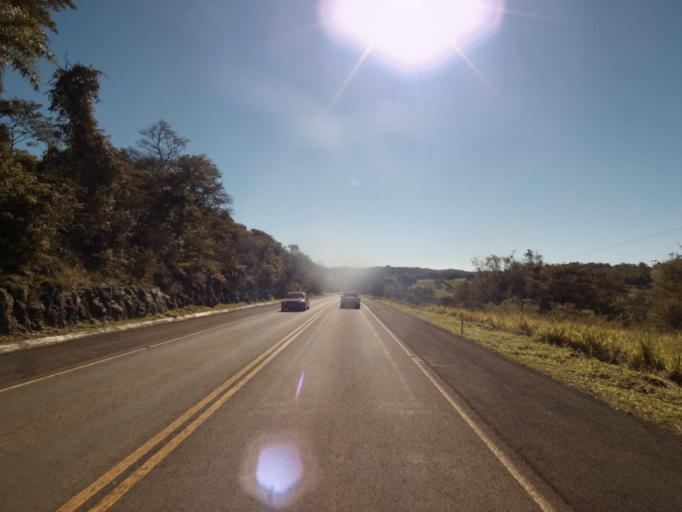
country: AR
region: Misiones
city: Bernardo de Irigoyen
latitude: -26.6953
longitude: -53.5381
